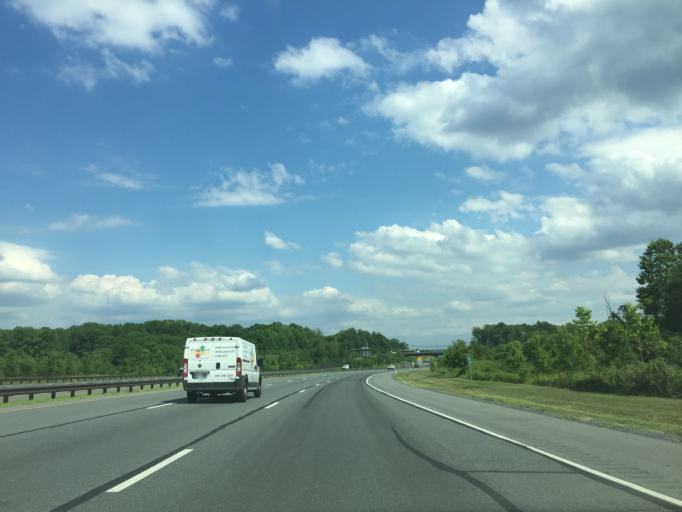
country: US
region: Maryland
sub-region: Montgomery County
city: Rossmoor
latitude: 39.1160
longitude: -77.0650
